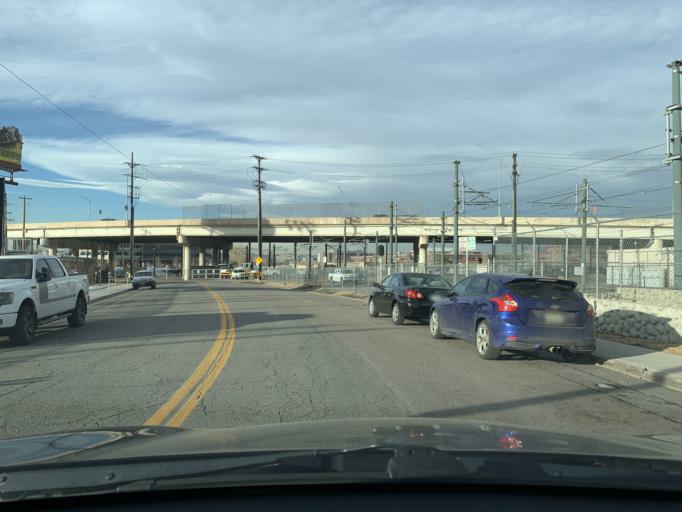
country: US
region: Colorado
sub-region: Denver County
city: Denver
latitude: 39.7394
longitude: -105.0071
